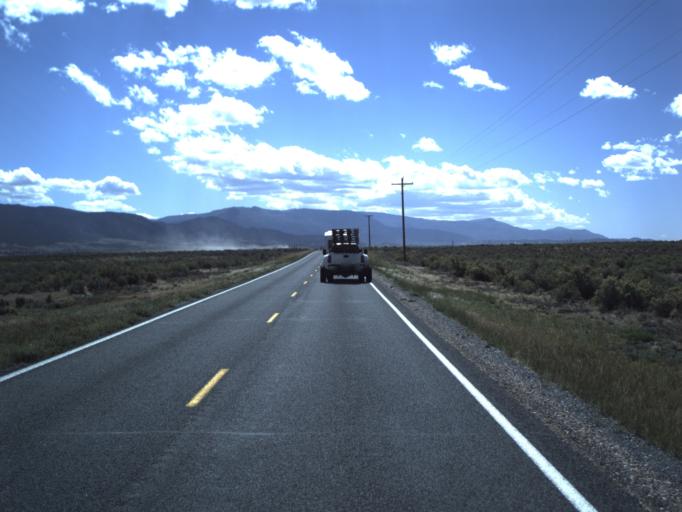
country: US
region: Utah
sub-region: Iron County
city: Enoch
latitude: 37.8267
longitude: -113.0504
